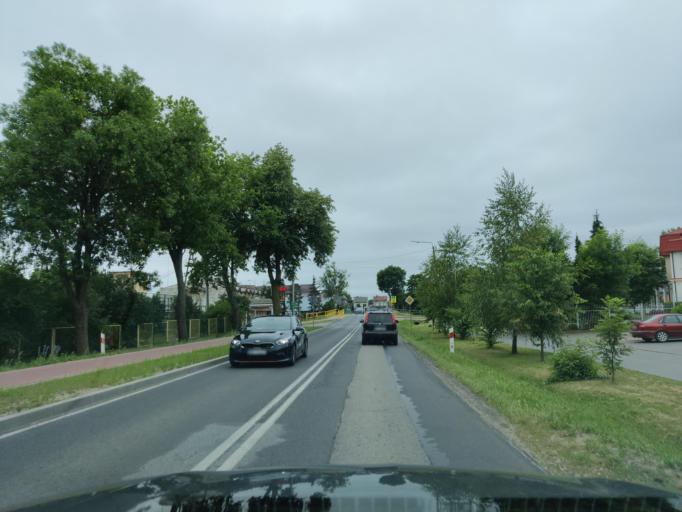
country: PL
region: Masovian Voivodeship
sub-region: Powiat ostrolecki
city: Myszyniec
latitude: 53.3877
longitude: 21.3415
